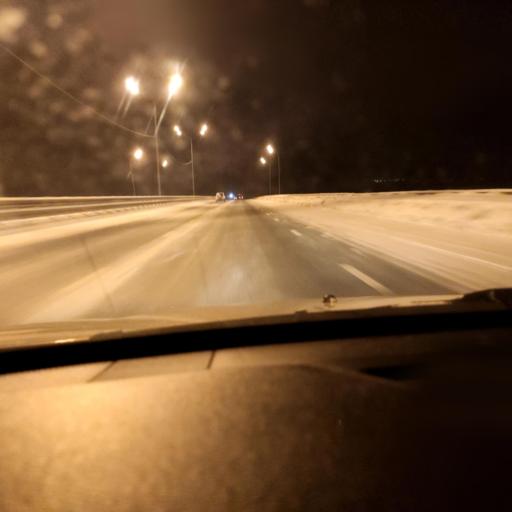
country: RU
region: Samara
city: Smyshlyayevka
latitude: 53.1768
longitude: 50.3095
